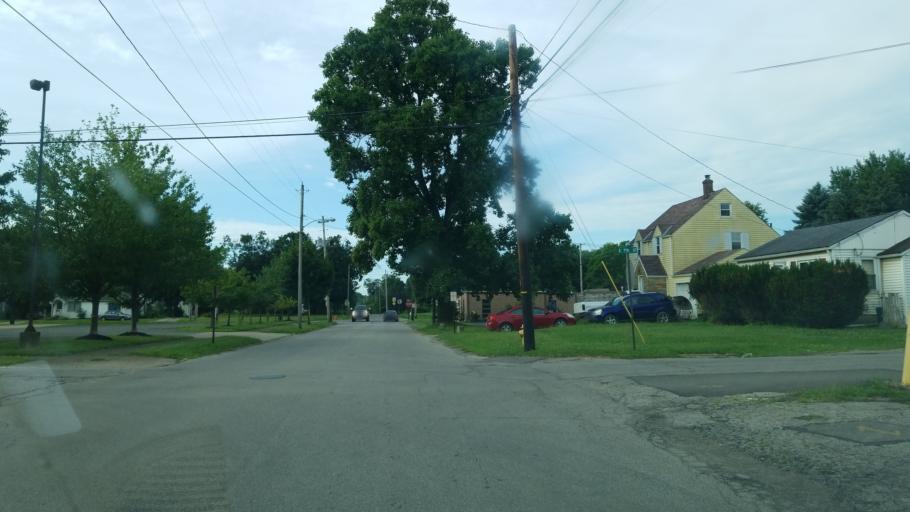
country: US
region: Ohio
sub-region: Ashland County
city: Ashland
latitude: 40.8730
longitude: -82.2962
